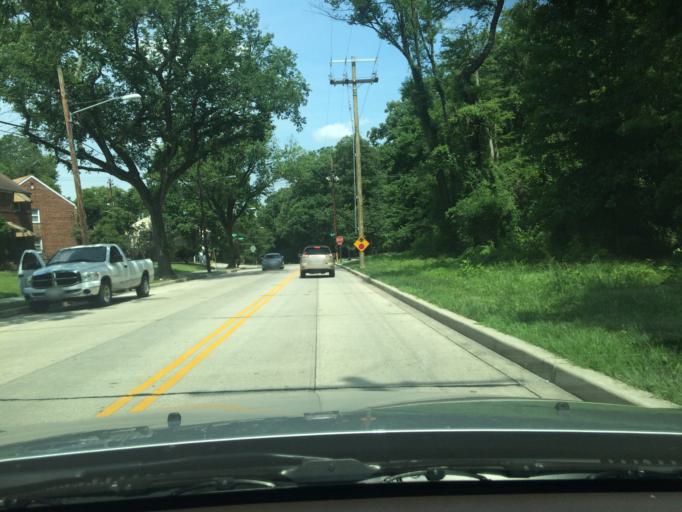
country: US
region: Maryland
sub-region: Prince George's County
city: Chillum
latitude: 38.9494
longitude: -76.9821
